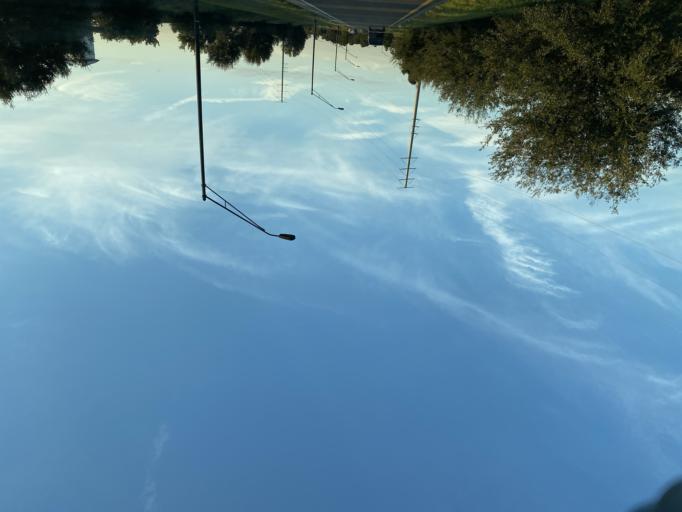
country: US
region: Florida
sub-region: Polk County
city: Citrus Ridge
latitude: 28.3759
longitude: -81.6126
